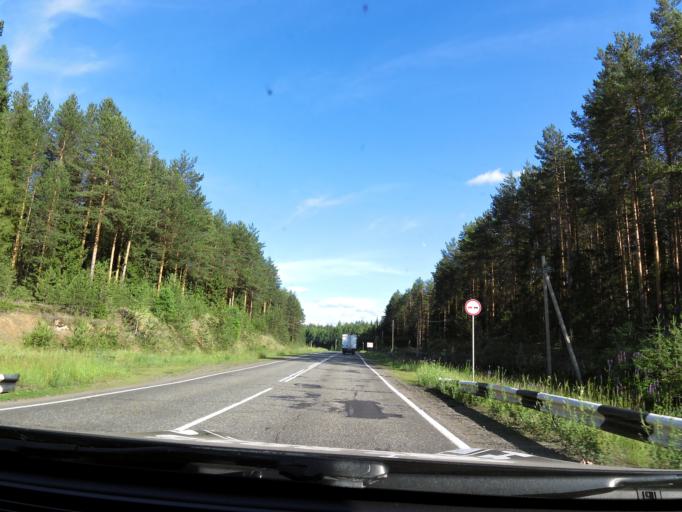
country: RU
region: Kirov
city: Dubrovka
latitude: 58.9055
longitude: 51.1867
